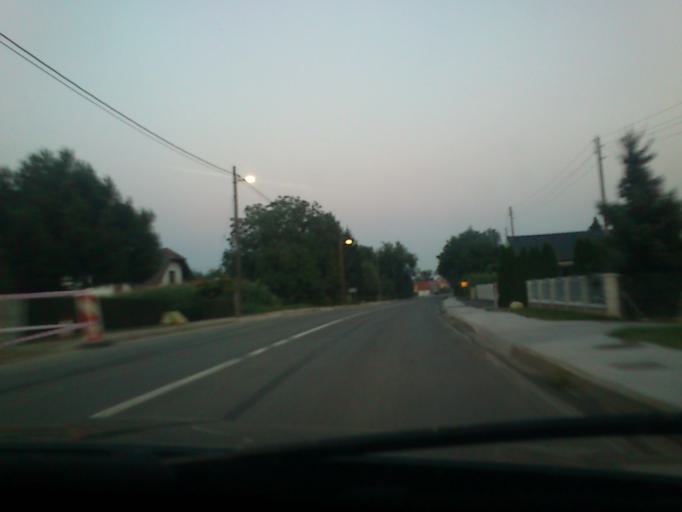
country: SI
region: Duplek
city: Spodnji Duplek
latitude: 46.4810
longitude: 15.7419
